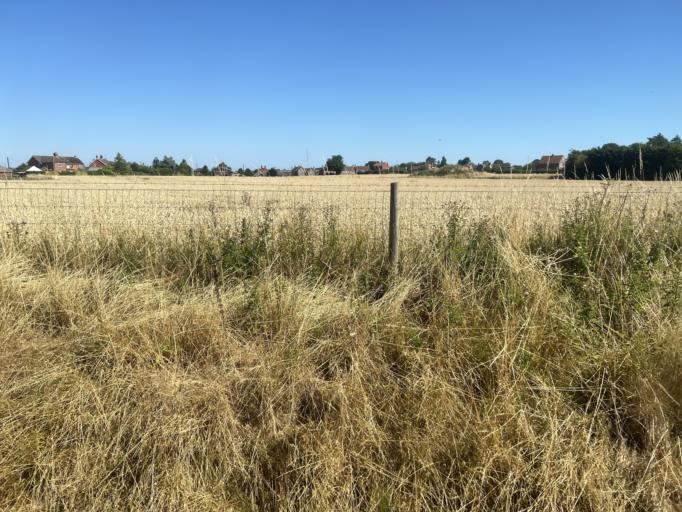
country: GB
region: England
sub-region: Lincolnshire
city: Wainfleet All Saints
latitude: 53.1077
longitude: 0.2292
